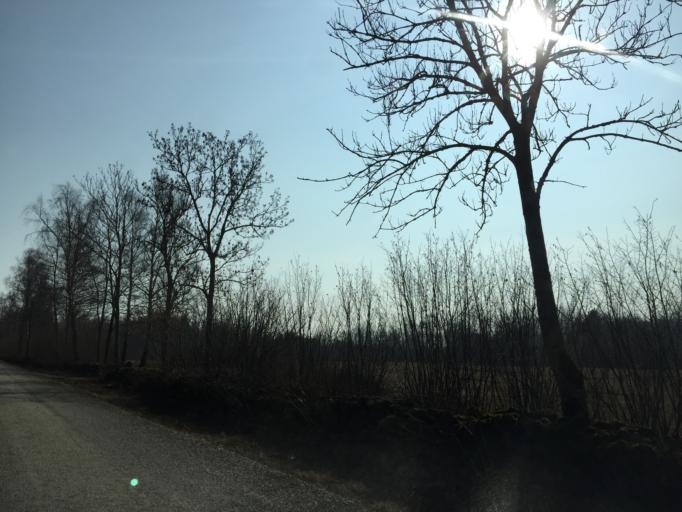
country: EE
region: Saare
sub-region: Orissaare vald
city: Orissaare
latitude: 58.5611
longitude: 23.2744
